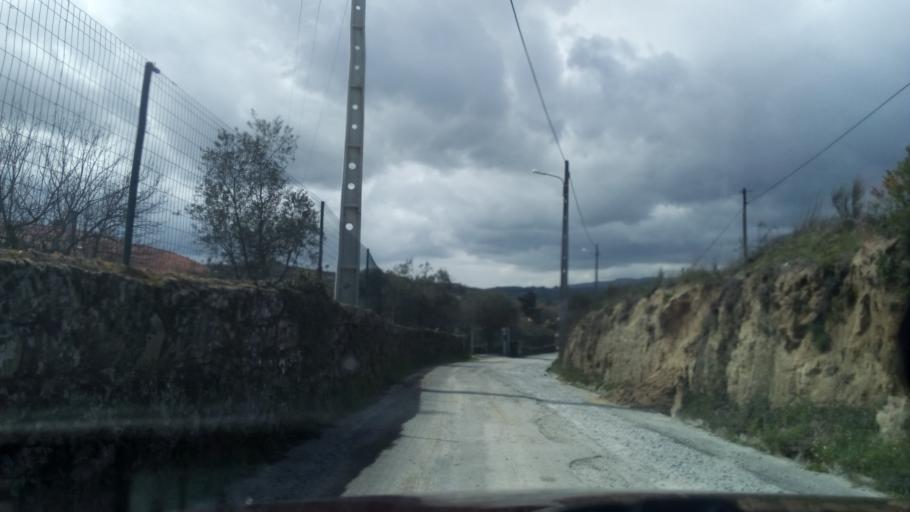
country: PT
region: Guarda
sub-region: Fornos de Algodres
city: Fornos de Algodres
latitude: 40.5839
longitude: -7.5478
